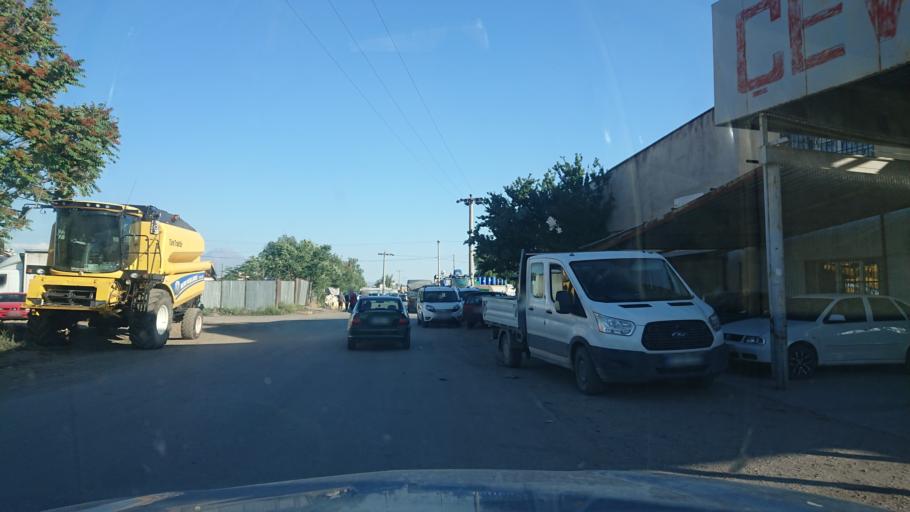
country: TR
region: Aksaray
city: Aksaray
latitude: 38.3752
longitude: 33.9917
